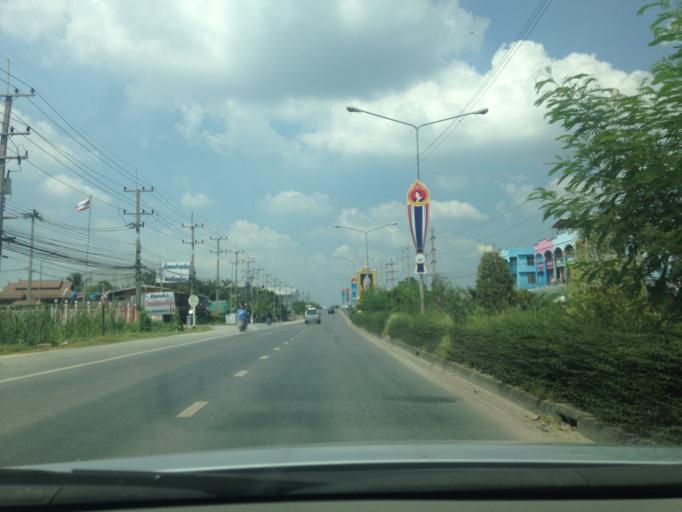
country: TH
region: Pathum Thani
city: Sam Khok
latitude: 14.0733
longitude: 100.5211
